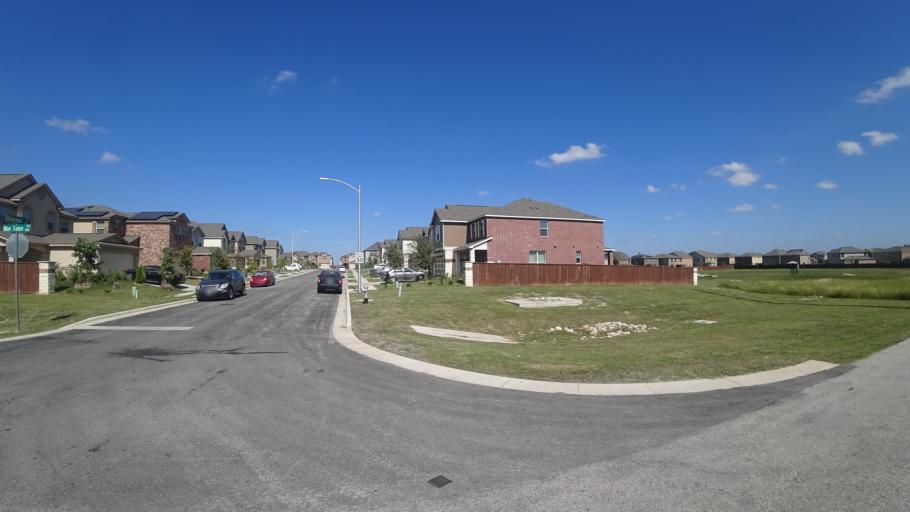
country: US
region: Texas
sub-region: Travis County
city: Manor
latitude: 30.3466
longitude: -97.6231
